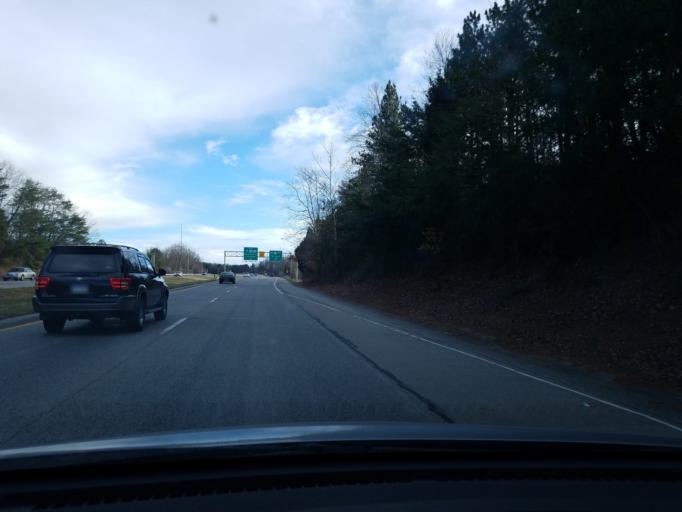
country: US
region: Indiana
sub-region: Floyd County
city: Galena
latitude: 38.3078
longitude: -85.8940
